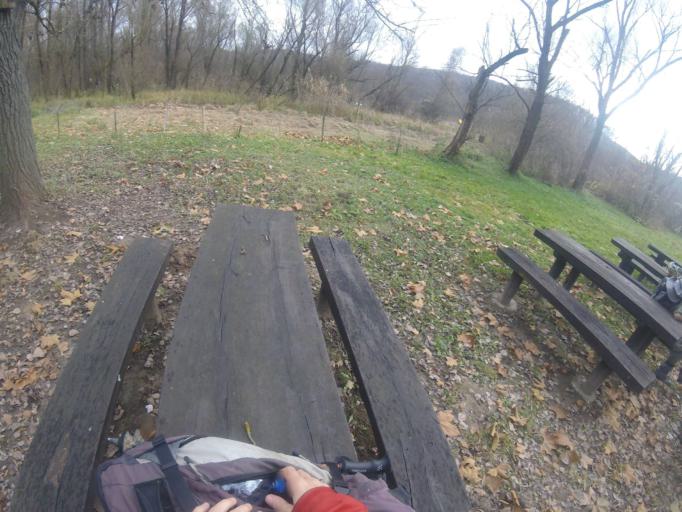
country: HU
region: Tolna
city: Szentgalpuszta
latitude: 46.2735
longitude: 18.6348
